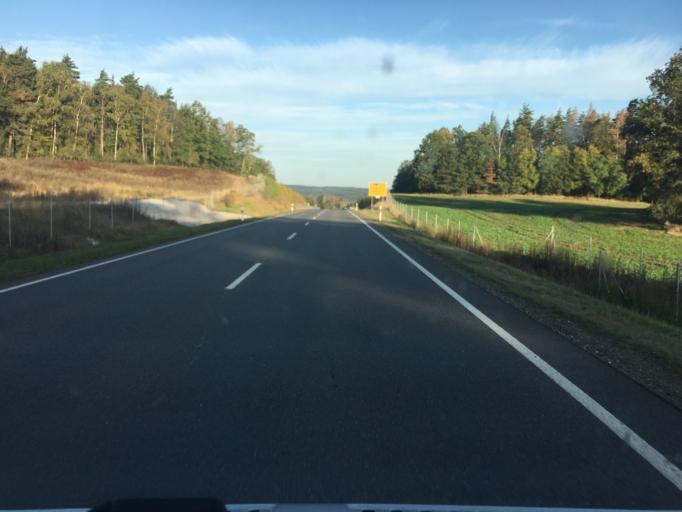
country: DE
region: Saxony
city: Kirchberg
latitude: 50.6134
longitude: 12.5062
